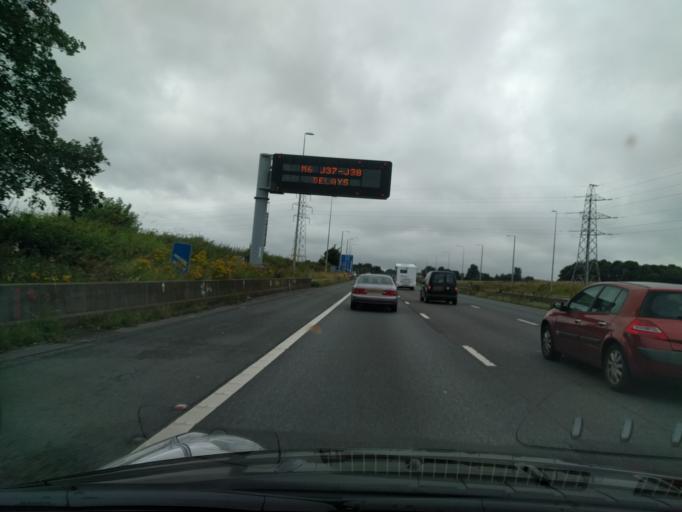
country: GB
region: England
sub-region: Warrington
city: Winwick
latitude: 53.4358
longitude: -2.5752
